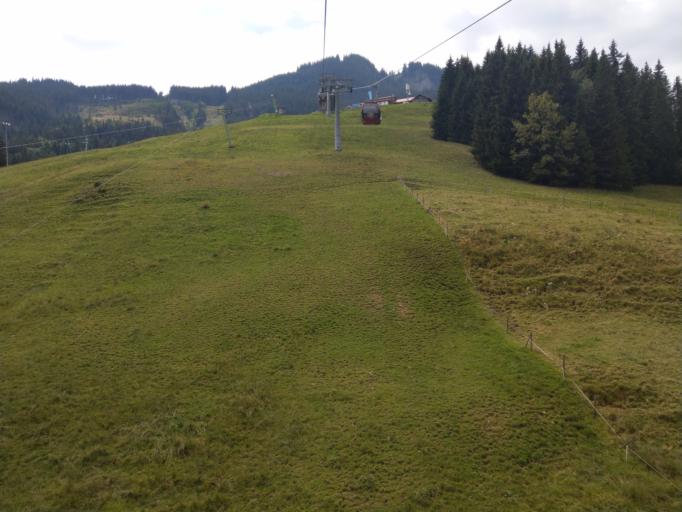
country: DE
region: Bavaria
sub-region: Swabia
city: Nesselwang
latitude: 47.6090
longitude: 10.4972
